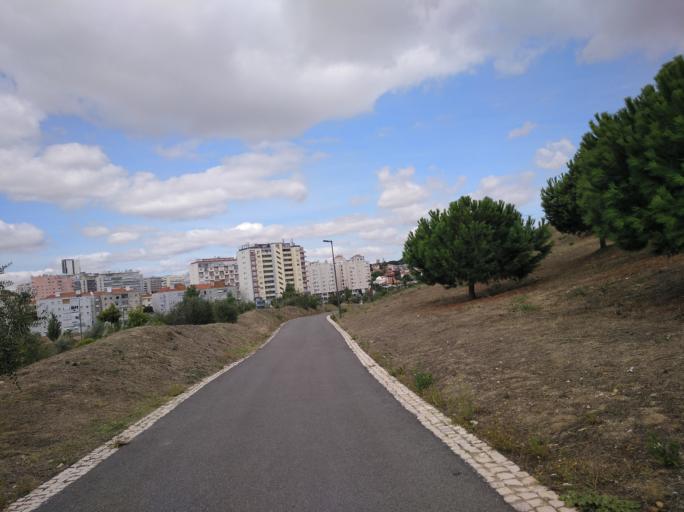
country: PT
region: Lisbon
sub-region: Lisbon
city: Lisbon
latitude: 38.7468
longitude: -9.1277
